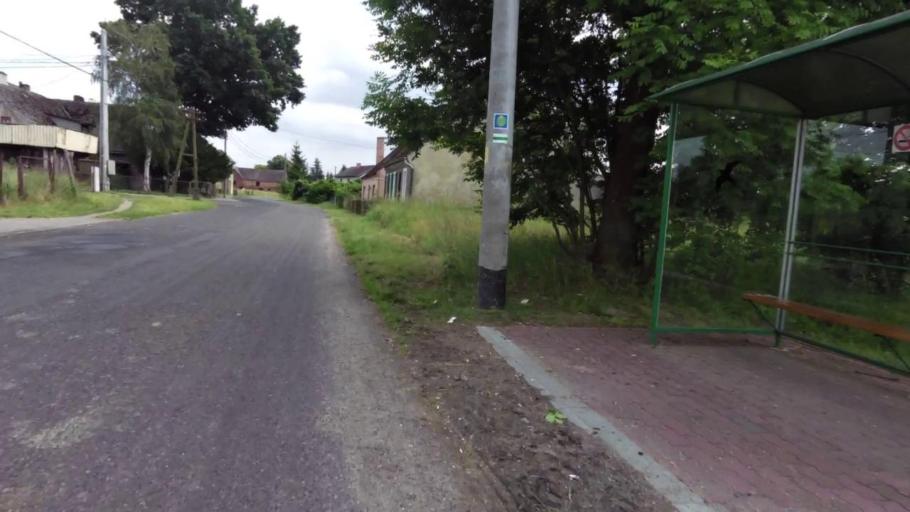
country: PL
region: West Pomeranian Voivodeship
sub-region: Powiat goleniowski
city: Stepnica
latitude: 53.6724
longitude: 14.5711
